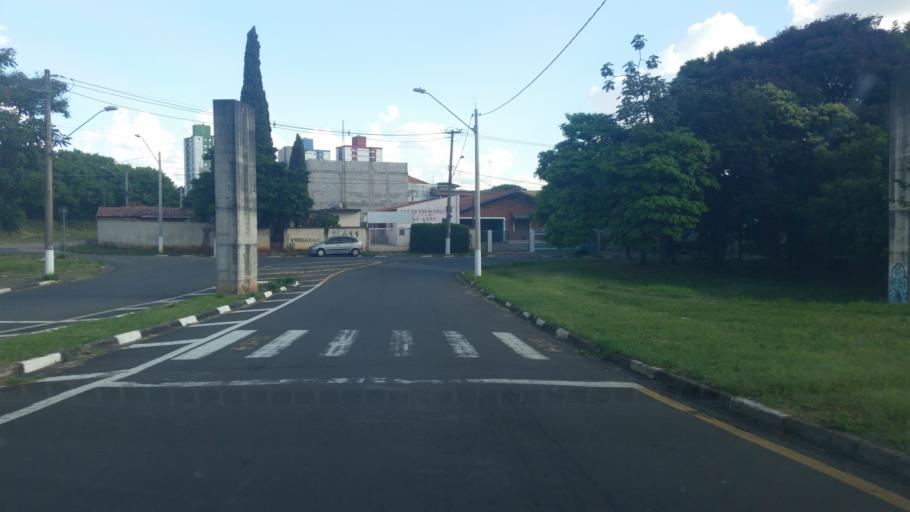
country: BR
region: Sao Paulo
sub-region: Campinas
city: Campinas
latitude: -22.8726
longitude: -47.0372
